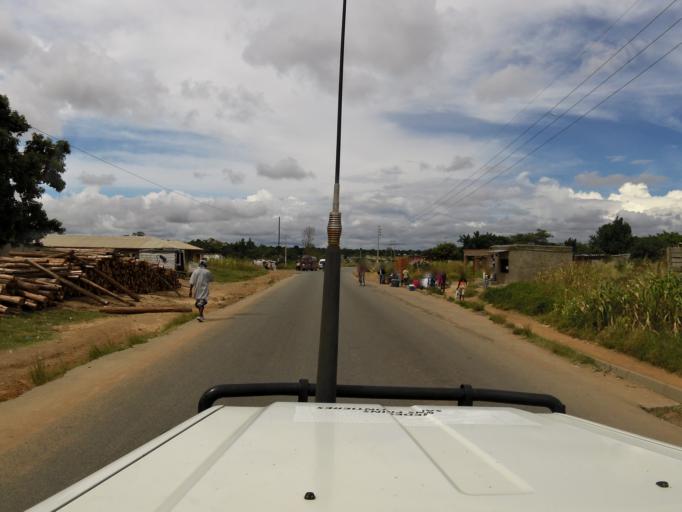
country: ZW
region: Harare
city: Epworth
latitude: -17.8902
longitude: 31.1395
